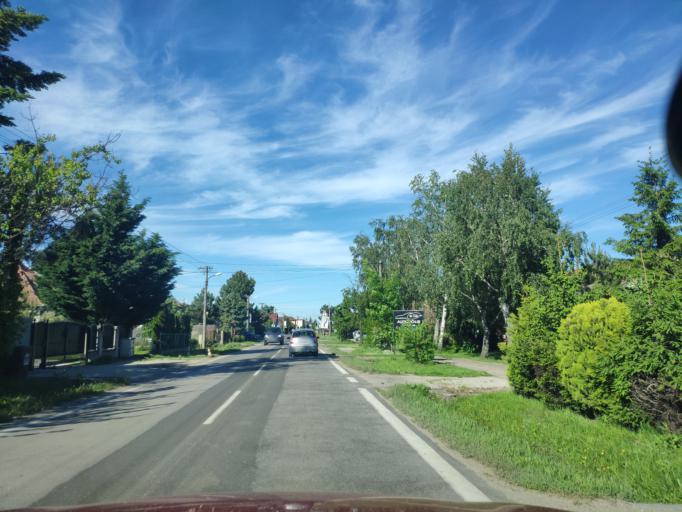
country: SK
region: Bratislavsky
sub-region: Okres Pezinok
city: Pezinok
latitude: 48.3048
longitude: 17.2849
